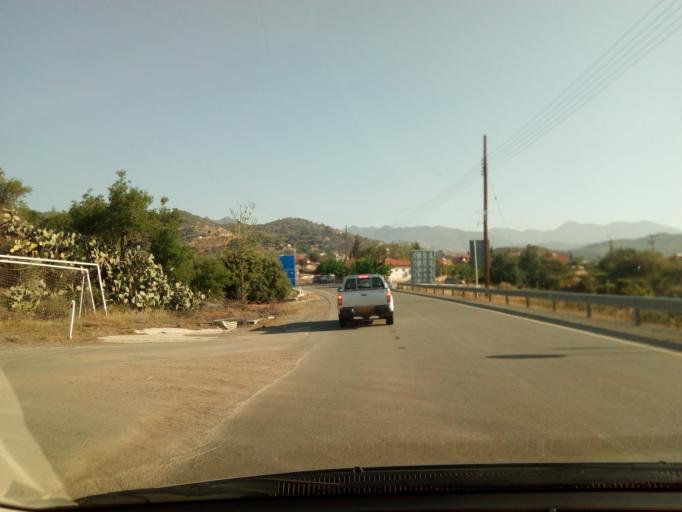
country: CY
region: Limassol
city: Parekklisha
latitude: 34.8441
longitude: 33.1539
